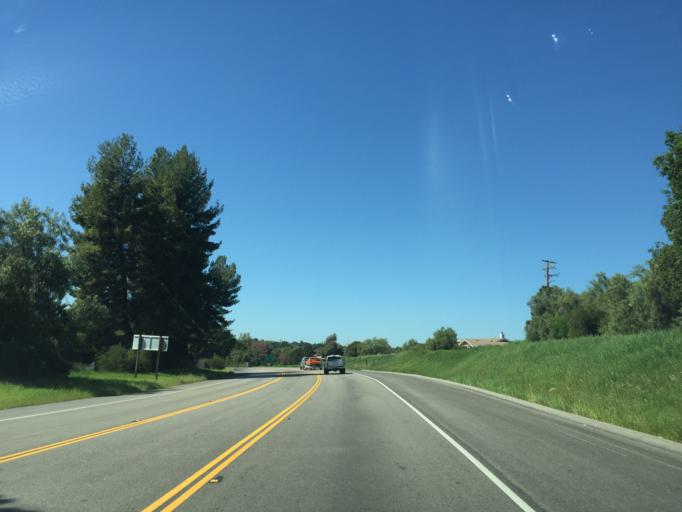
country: US
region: California
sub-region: Santa Barbara County
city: Los Olivos
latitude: 34.6666
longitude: -120.1116
